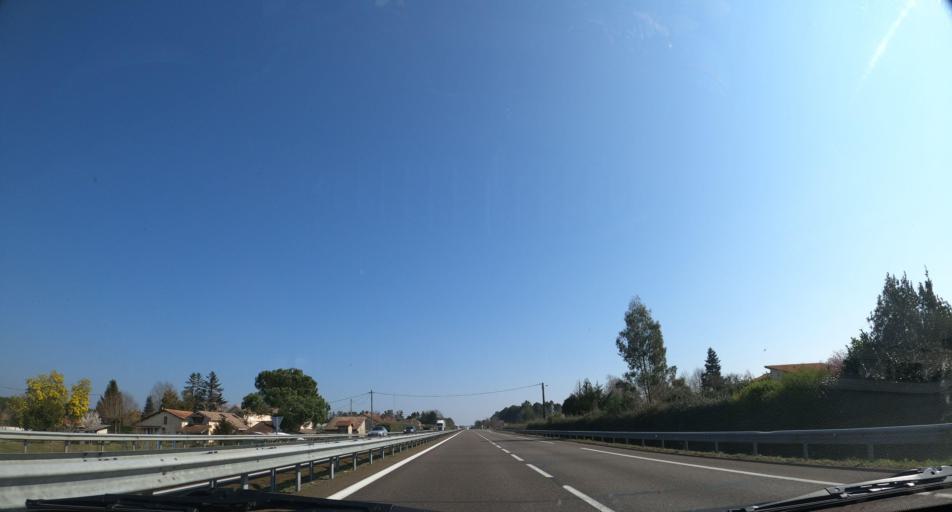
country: FR
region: Aquitaine
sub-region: Departement des Landes
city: Saint-Perdon
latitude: 43.8713
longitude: -0.5934
